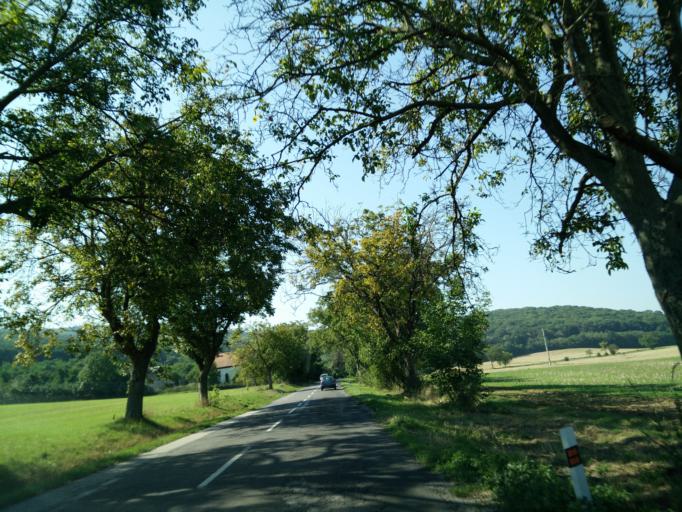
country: SK
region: Nitriansky
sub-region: Okres Nitra
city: Nitra
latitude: 48.3745
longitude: 18.0909
